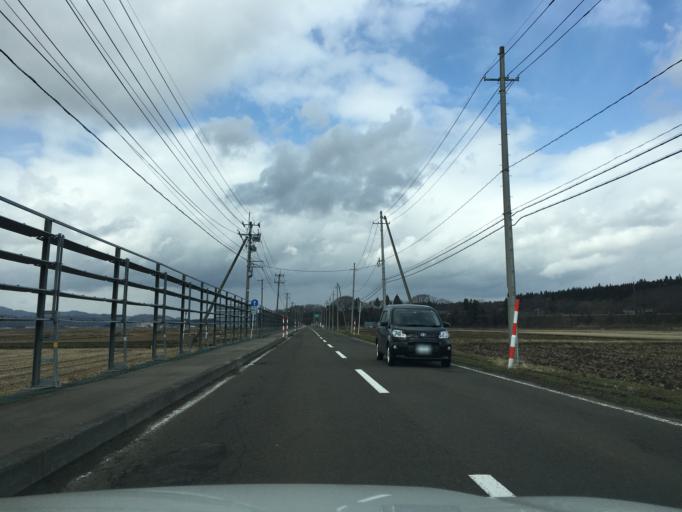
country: JP
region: Akita
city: Takanosu
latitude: 40.1379
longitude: 140.3526
